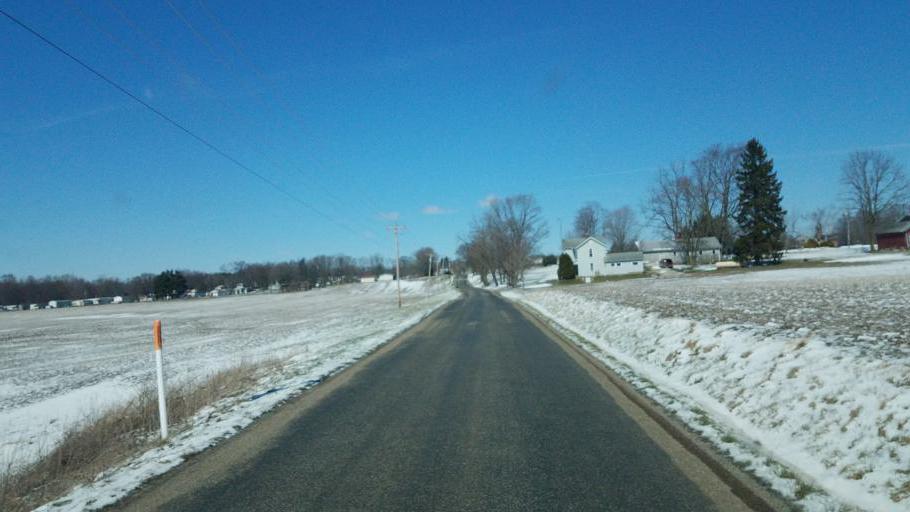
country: US
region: Ohio
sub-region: Richland County
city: Lexington
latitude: 40.6312
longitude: -82.6086
